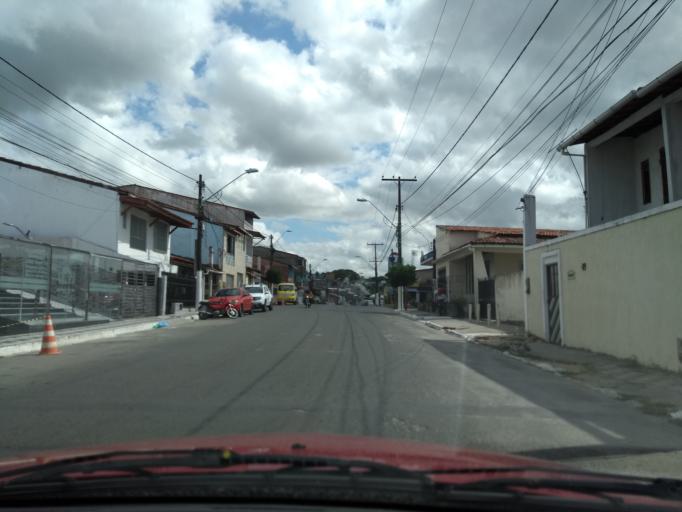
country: BR
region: Bahia
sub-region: Sao Francisco Do Conde
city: Sao Francisco do Conde
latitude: -12.6255
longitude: -38.6755
